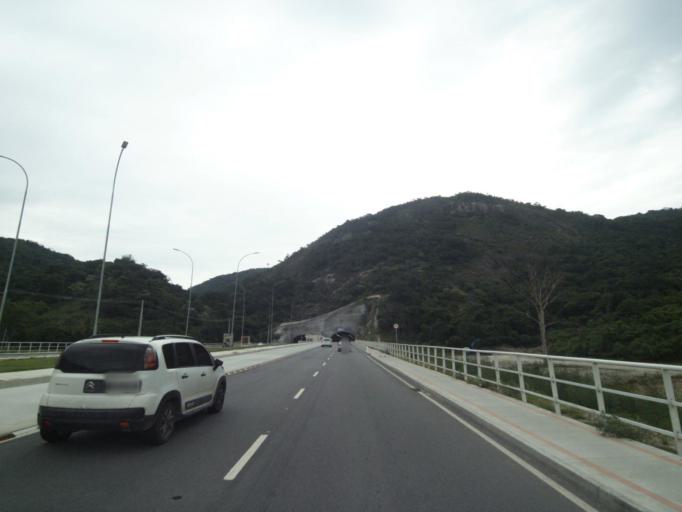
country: BR
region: Rio de Janeiro
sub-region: Niteroi
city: Niteroi
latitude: -22.9362
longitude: -43.0822
